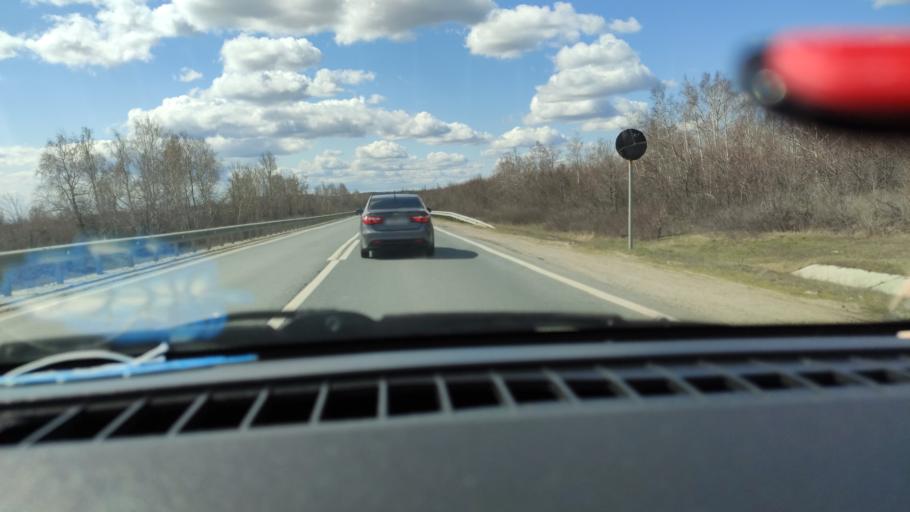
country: RU
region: Saratov
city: Dukhovnitskoye
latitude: 52.6738
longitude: 48.2249
